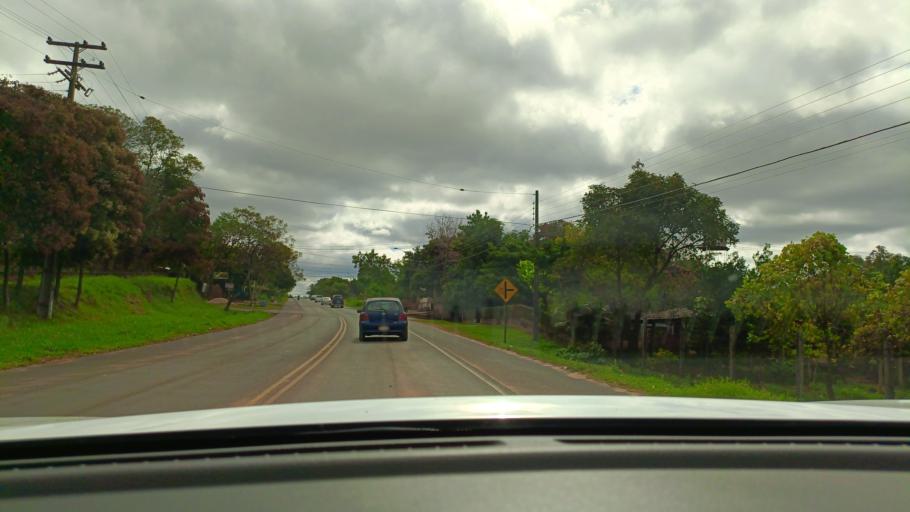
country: PY
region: San Pedro
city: Guayaybi
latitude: -24.6646
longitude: -56.4560
